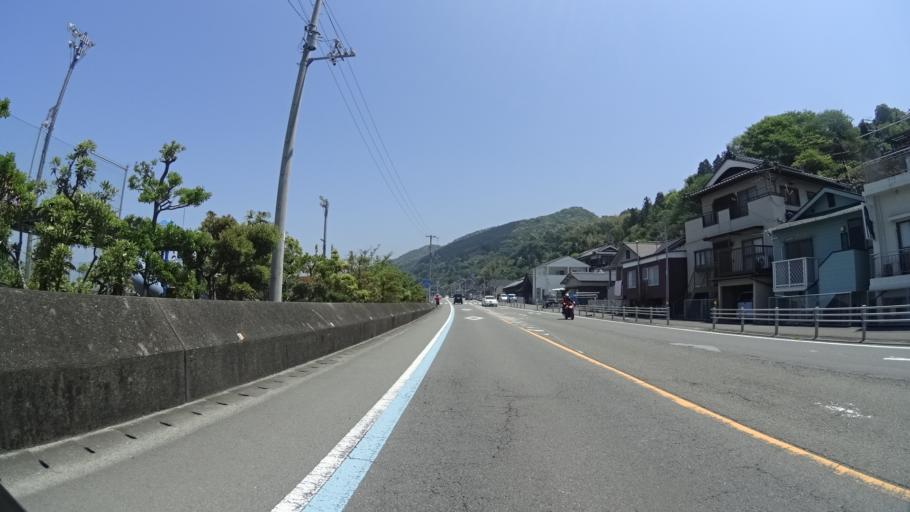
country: JP
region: Ehime
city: Ozu
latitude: 33.6520
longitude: 132.5802
